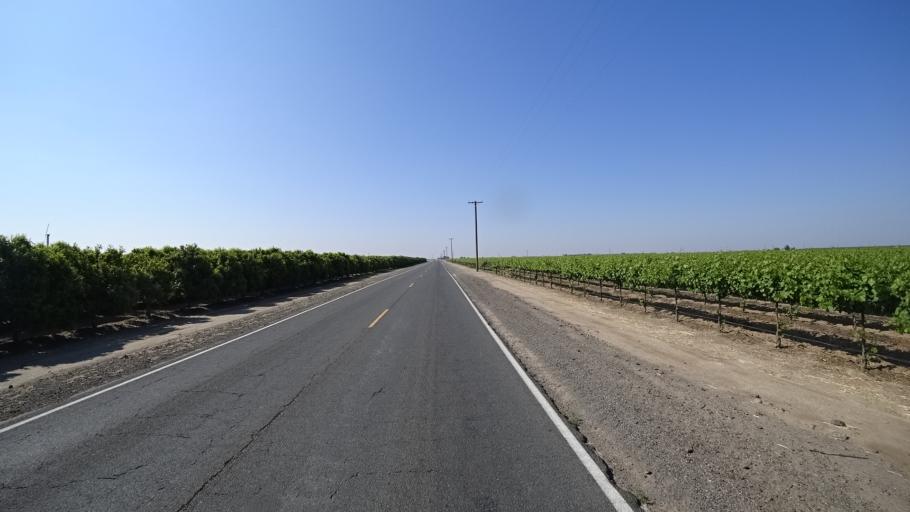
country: US
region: California
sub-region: Kings County
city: Lucerne
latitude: 36.3902
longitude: -119.5650
